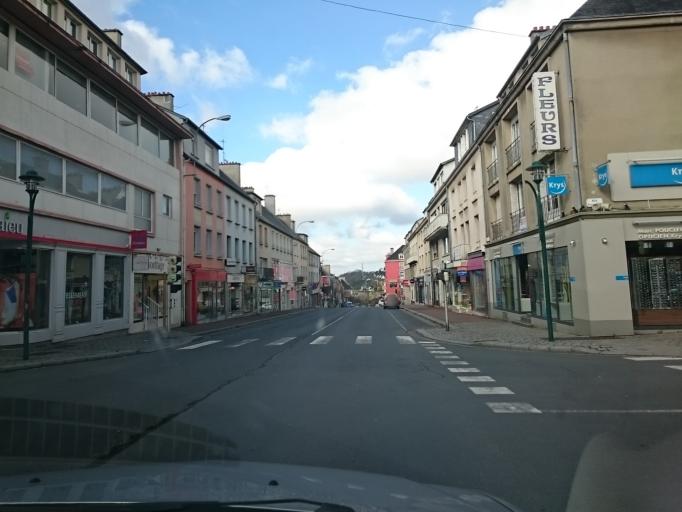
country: FR
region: Lower Normandy
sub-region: Departement de la Manche
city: Saint-Lo
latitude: 49.1150
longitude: -1.0885
